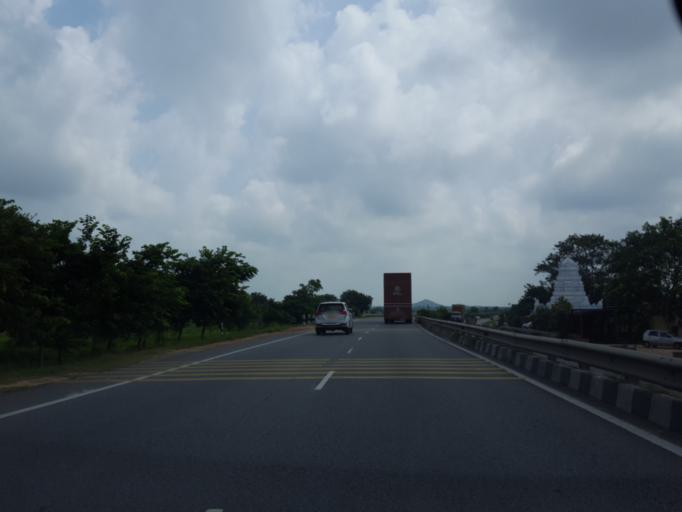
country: IN
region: Telangana
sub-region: Nalgonda
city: Bhongir
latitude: 17.2302
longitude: 79.0067
